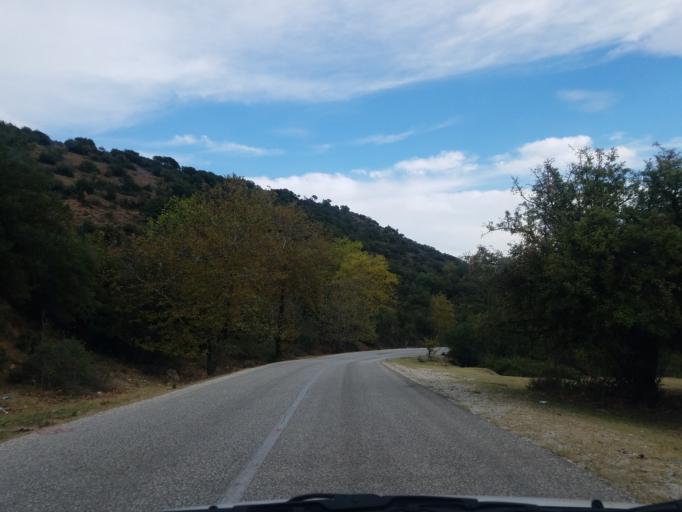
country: GR
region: Thessaly
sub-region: Trikala
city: Kalampaka
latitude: 39.7159
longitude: 21.6485
